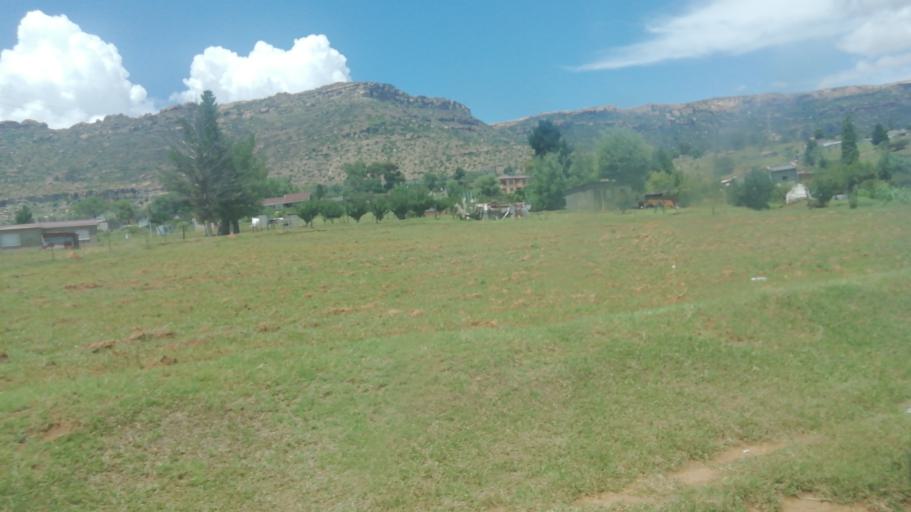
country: LS
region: Maseru
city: Nako
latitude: -29.6198
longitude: 27.5180
